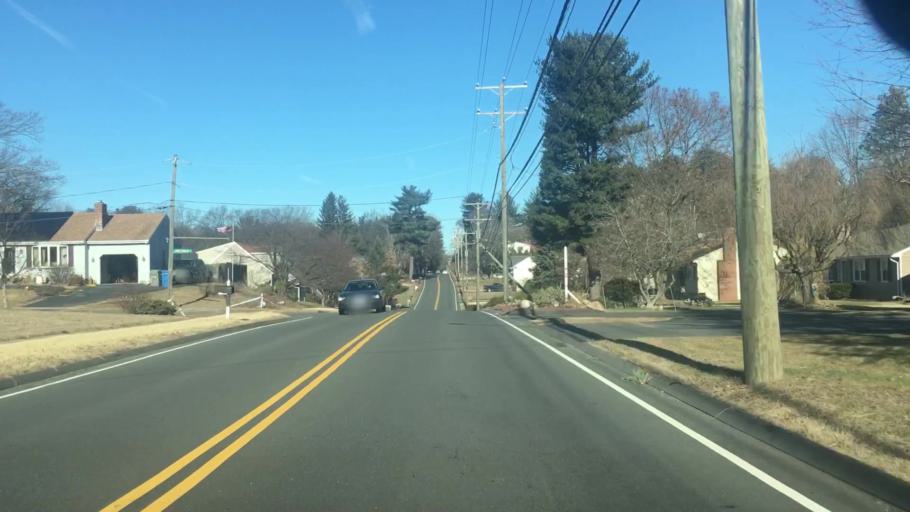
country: US
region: Connecticut
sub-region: Hartford County
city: Plainville
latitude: 41.6594
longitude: -72.9011
